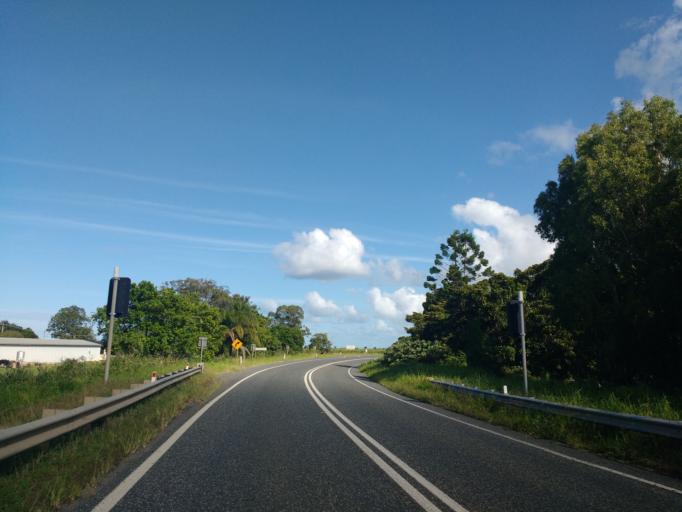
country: AU
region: New South Wales
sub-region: Ballina
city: Ballina
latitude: -28.9550
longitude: 153.4651
